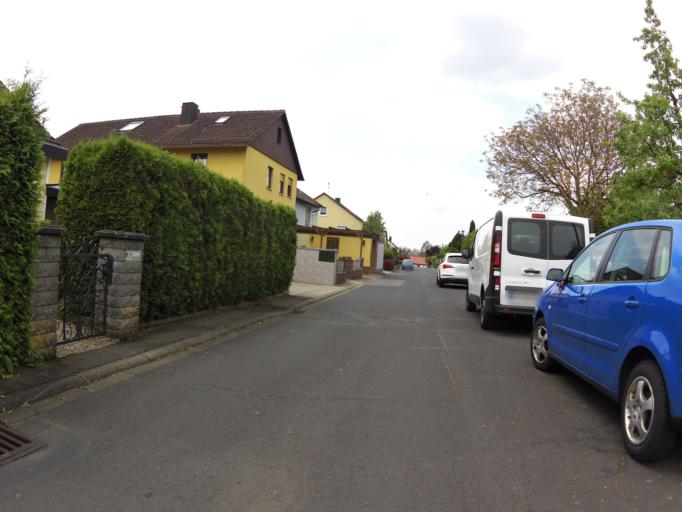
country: DE
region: Bavaria
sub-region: Regierungsbezirk Unterfranken
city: Kurnach
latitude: 49.8492
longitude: 10.0451
